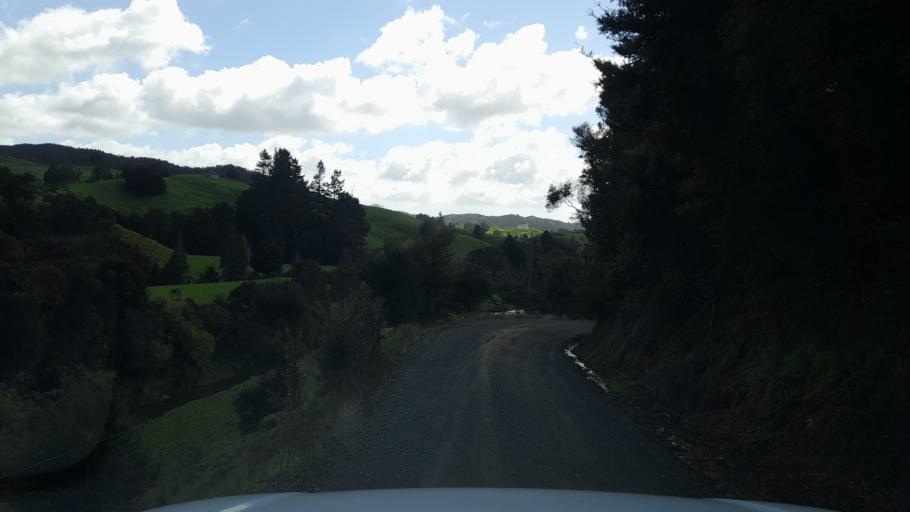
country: NZ
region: Northland
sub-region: Far North District
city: Waimate North
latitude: -35.1591
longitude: 173.7123
